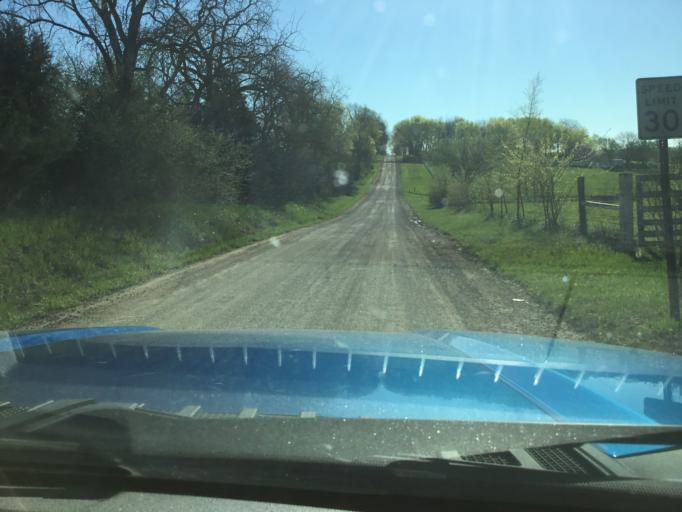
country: US
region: Kansas
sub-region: Douglas County
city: Lawrence
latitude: 38.9931
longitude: -95.3535
